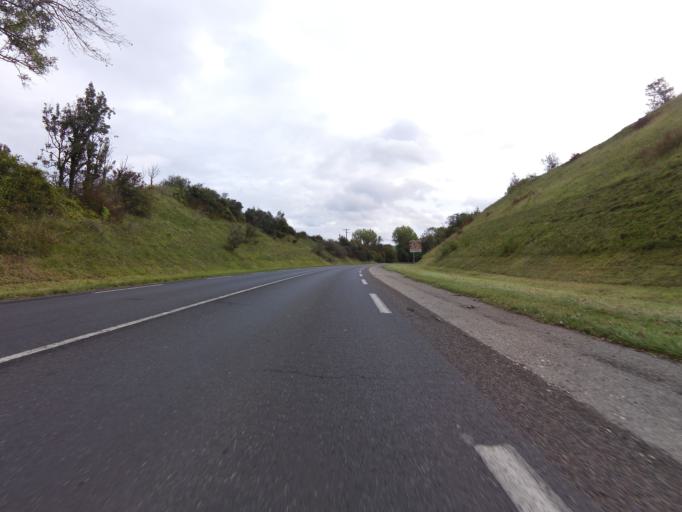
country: FR
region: Haute-Normandie
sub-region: Departement de la Seine-Maritime
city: Criel-sur-Mer
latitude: 50.0123
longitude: 1.3098
